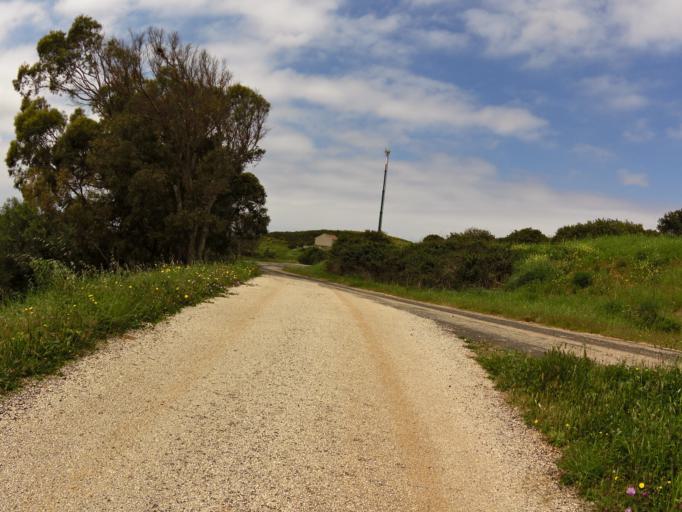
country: PT
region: Faro
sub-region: Vila do Bispo
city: Vila do Bispo
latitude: 37.0814
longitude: -8.8838
